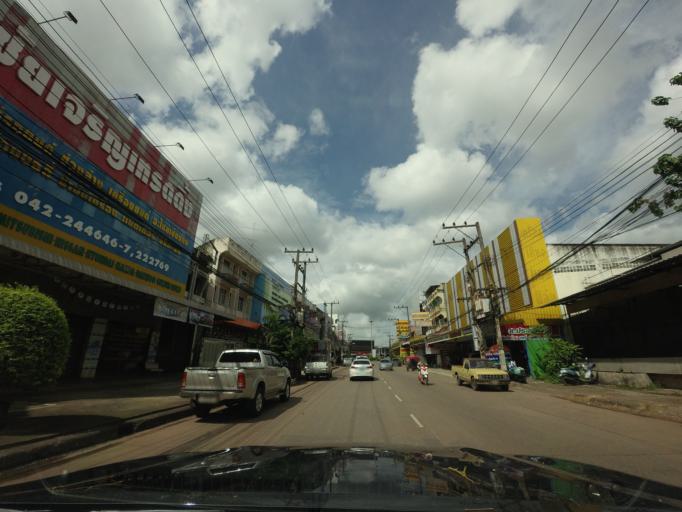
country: TH
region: Changwat Udon Thani
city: Udon Thani
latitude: 17.4010
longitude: 102.7965
